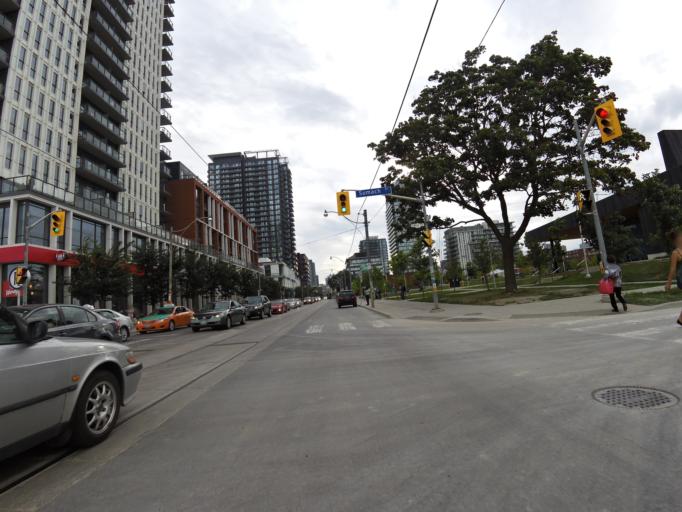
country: CA
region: Ontario
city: Toronto
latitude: 43.6607
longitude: -79.3604
